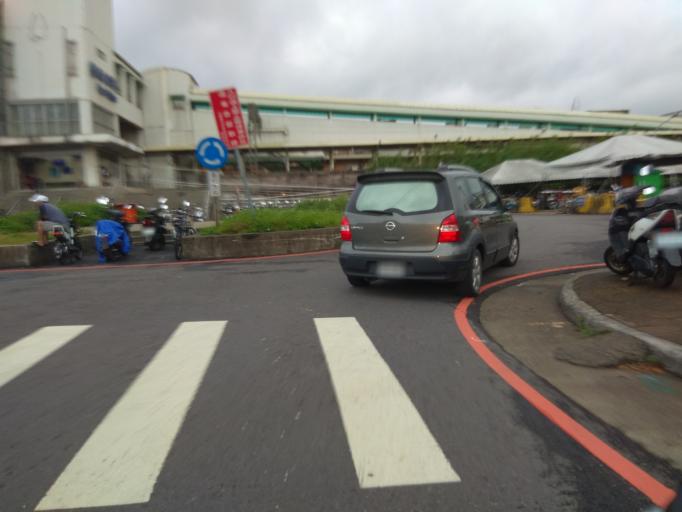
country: TW
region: Taiwan
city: Daxi
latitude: 24.9199
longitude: 121.1829
